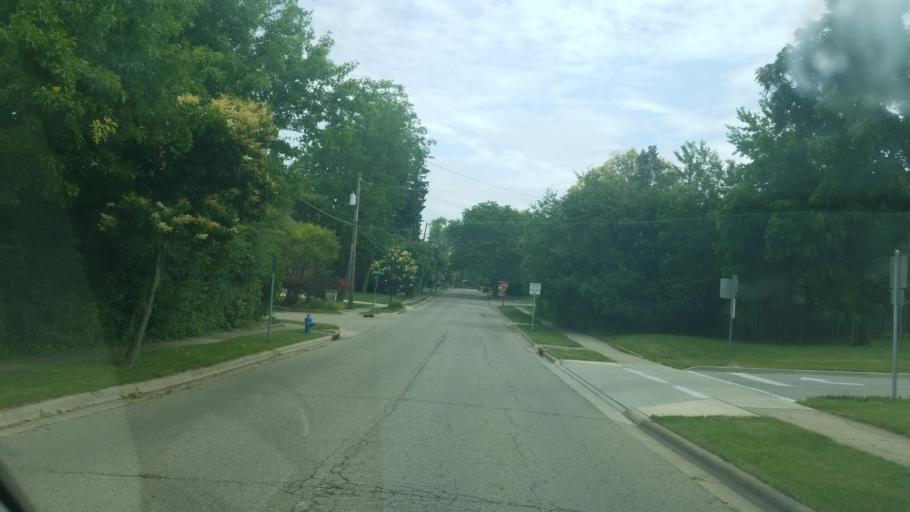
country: US
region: Ohio
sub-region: Franklin County
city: Worthington
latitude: 40.0982
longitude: -83.0081
